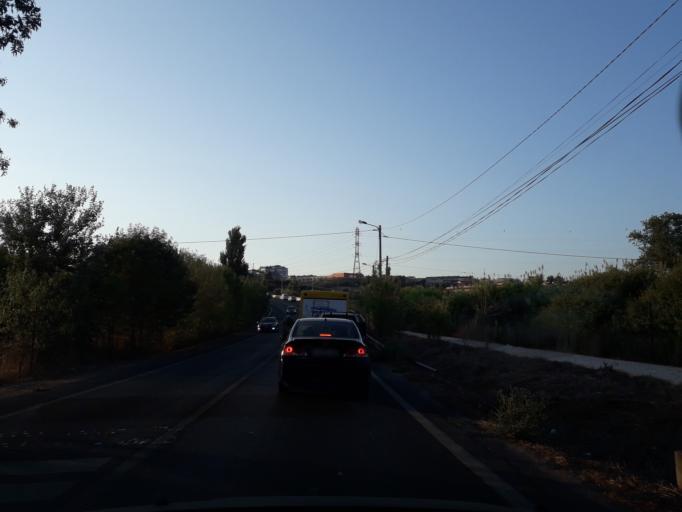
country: PT
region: Lisbon
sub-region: Odivelas
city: Pontinha
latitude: 38.7740
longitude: -9.2045
